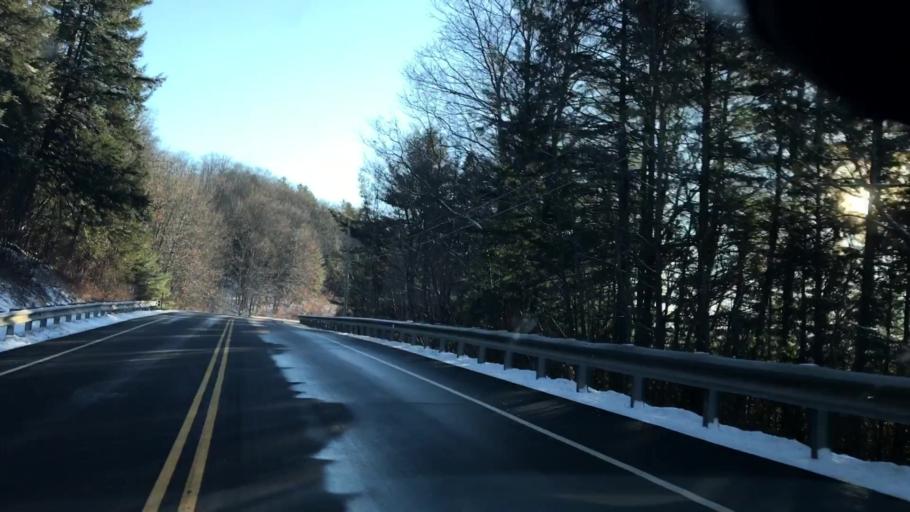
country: US
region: New Hampshire
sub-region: Grafton County
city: Orford
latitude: 43.9556
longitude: -72.0984
